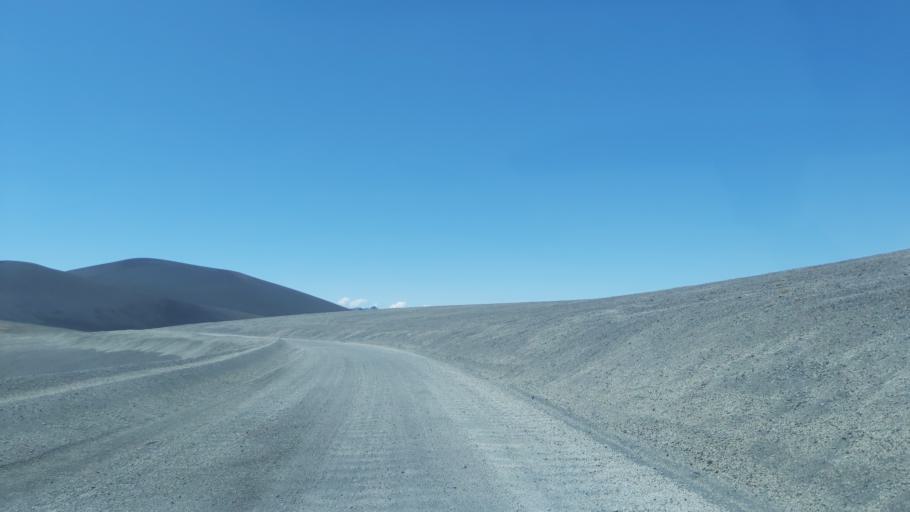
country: CL
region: Araucania
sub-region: Provincia de Cautin
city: Vilcun
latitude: -38.3779
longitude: -71.5427
